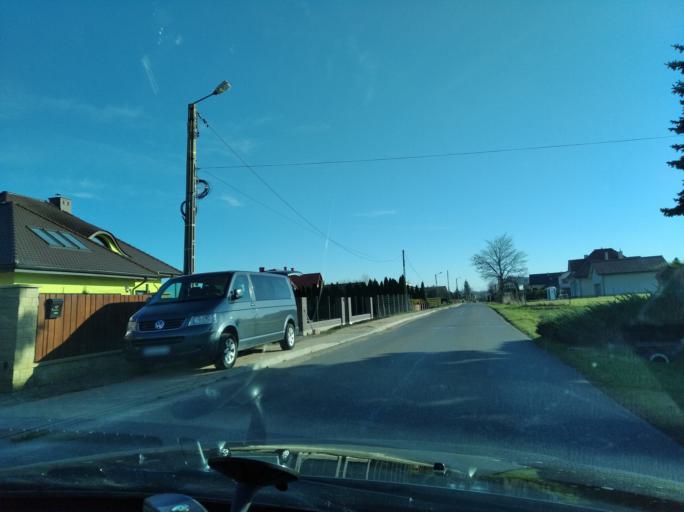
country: PL
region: Subcarpathian Voivodeship
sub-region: Powiat rzeszowski
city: Lutoryz
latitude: 49.9799
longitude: 21.9243
